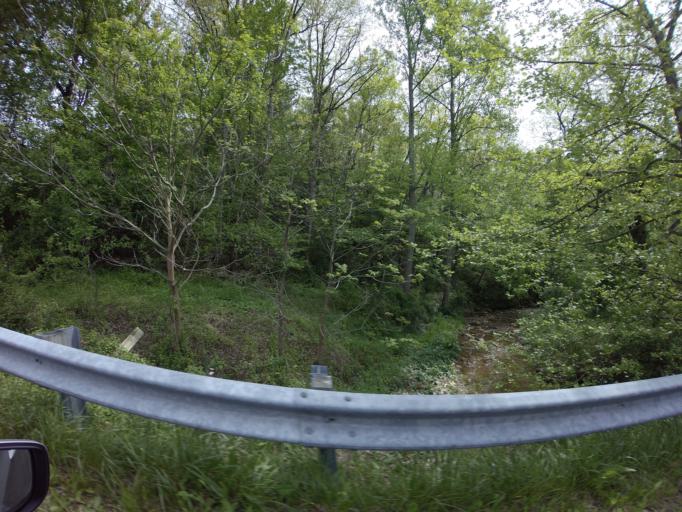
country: US
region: Maryland
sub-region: Carroll County
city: Eldersburg
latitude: 39.4711
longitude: -76.9701
